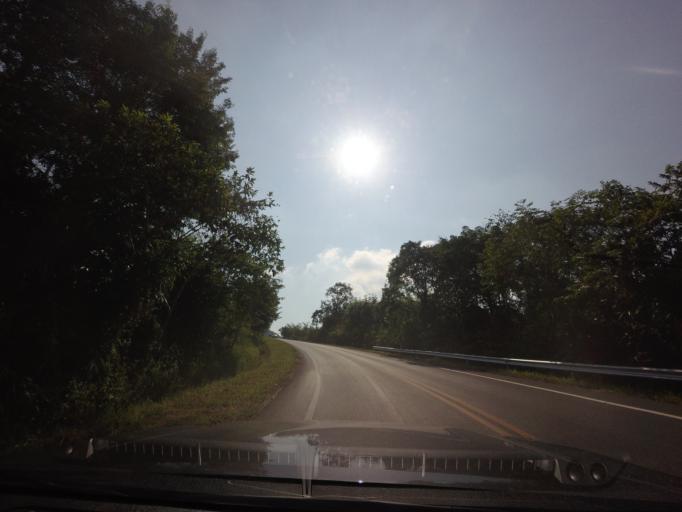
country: TH
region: Nan
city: Santi Suk
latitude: 18.9211
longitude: 100.8915
